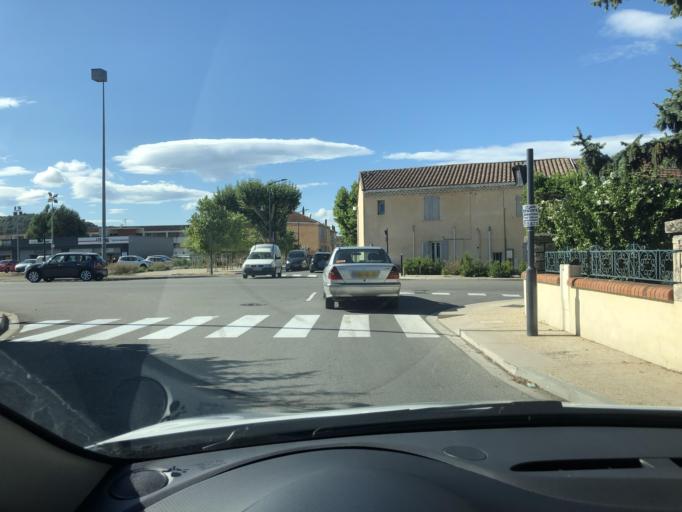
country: FR
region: Provence-Alpes-Cote d'Azur
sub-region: Departement des Bouches-du-Rhone
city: Chateaurenard
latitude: 43.8877
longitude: 4.8485
